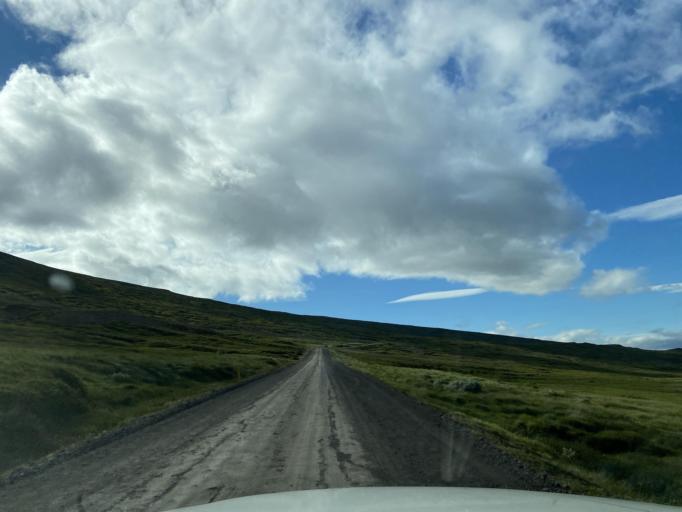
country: IS
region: East
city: Egilsstadir
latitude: 65.1883
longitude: -14.3321
